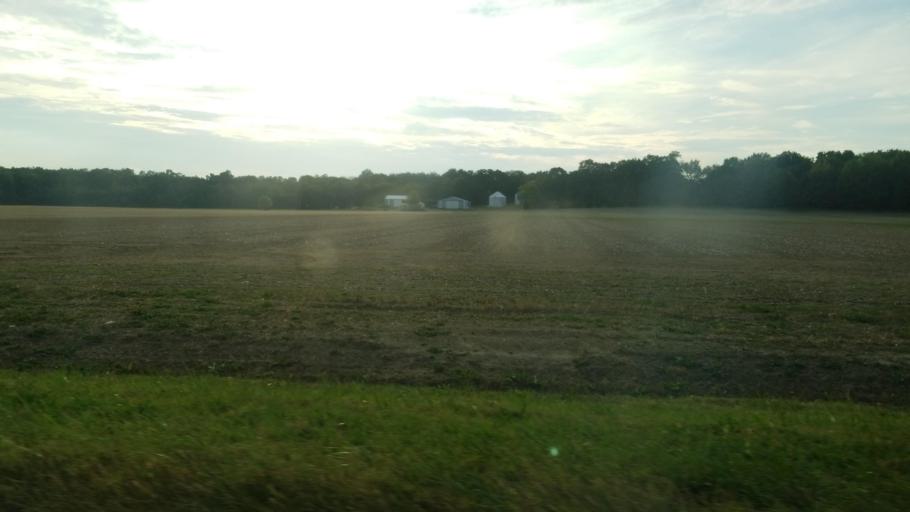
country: US
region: Illinois
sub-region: Saline County
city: Harrisburg
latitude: 37.7883
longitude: -88.5404
